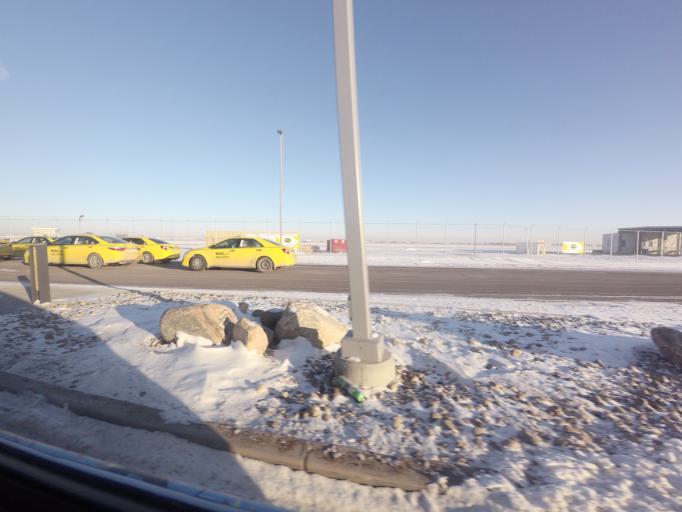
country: CA
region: Saskatchewan
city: Saskatoon
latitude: 52.1707
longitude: -106.6879
